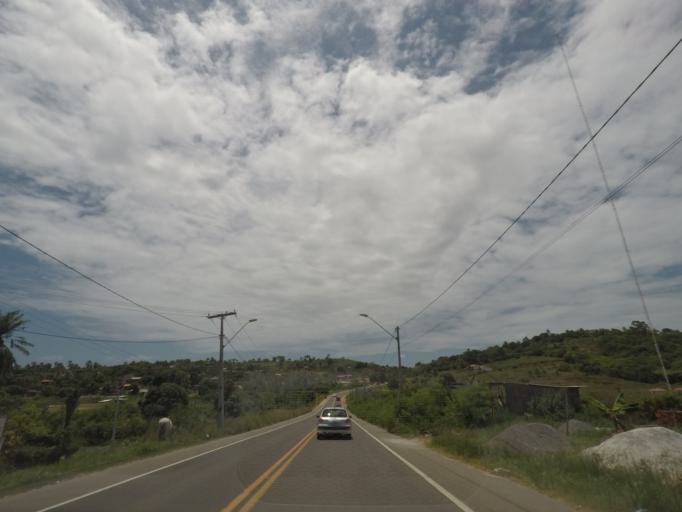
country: BR
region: Bahia
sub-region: Itaparica
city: Itaparica
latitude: -12.9351
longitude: -38.6244
